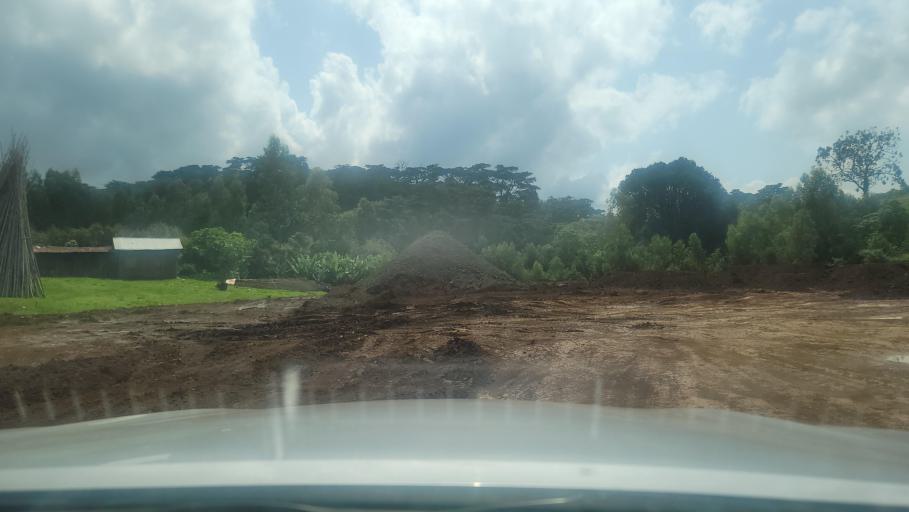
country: ET
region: Oromiya
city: Agaro
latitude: 7.7981
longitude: 36.4577
